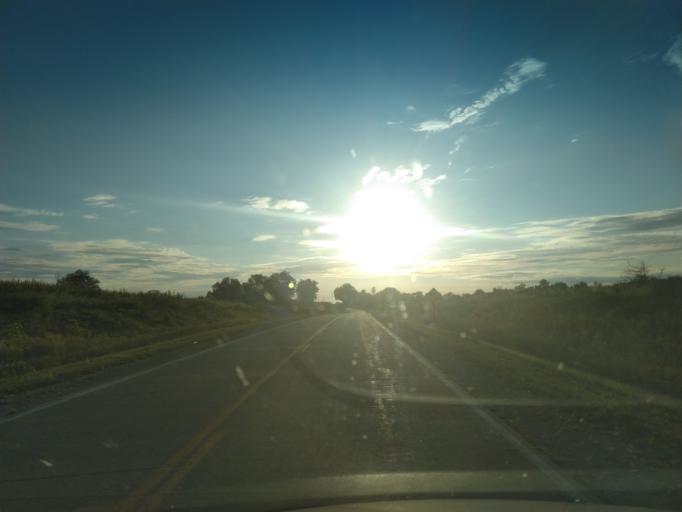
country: US
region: Iowa
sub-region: Jackson County
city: Maquoketa
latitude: 42.1643
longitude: -90.6947
